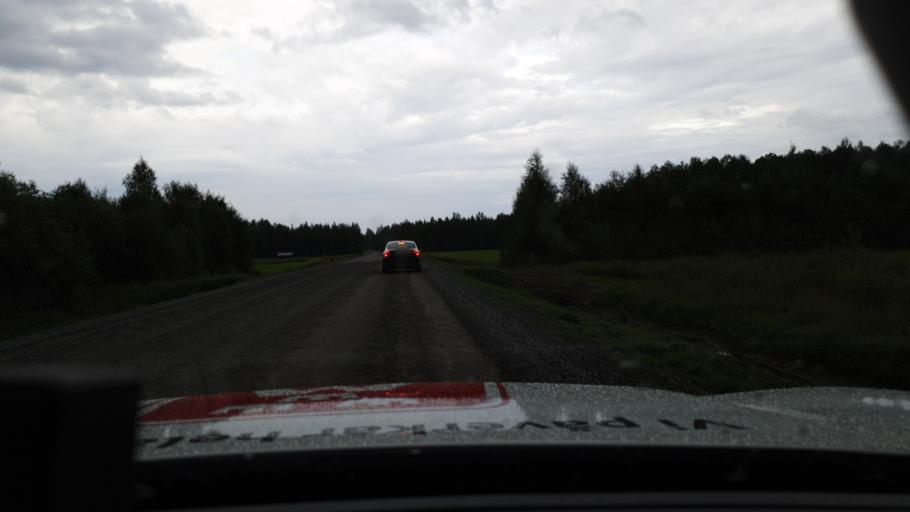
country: SE
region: Norrbotten
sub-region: Bodens Kommun
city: Boden
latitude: 65.8506
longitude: 21.5250
